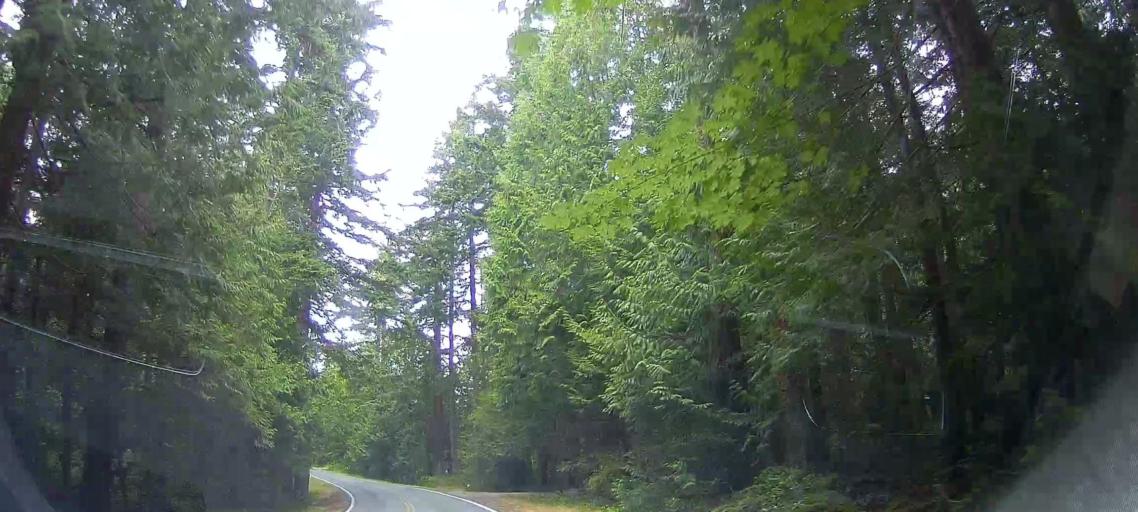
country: US
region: Washington
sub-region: Skagit County
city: Anacortes
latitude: 48.4798
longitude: -122.6257
